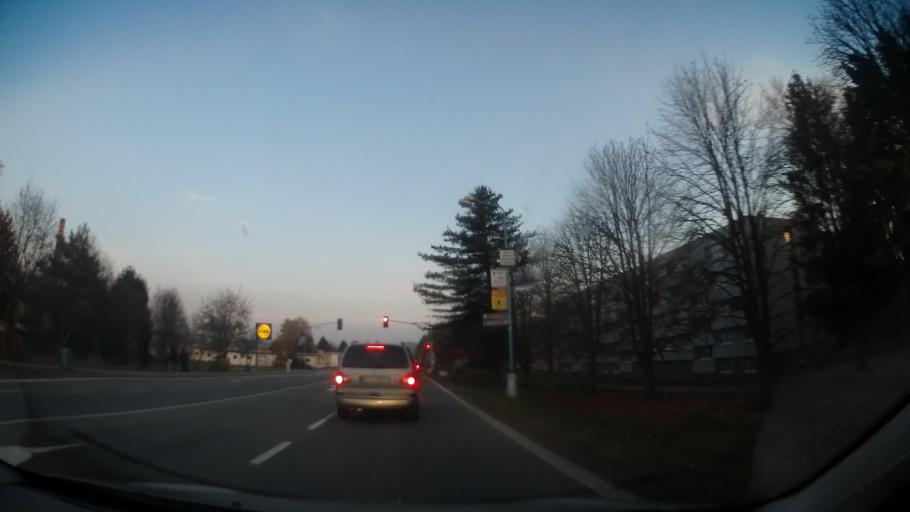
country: CZ
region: Vysocina
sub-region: Okres Pelhrimov
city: Pelhrimov
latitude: 49.4375
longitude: 15.2136
